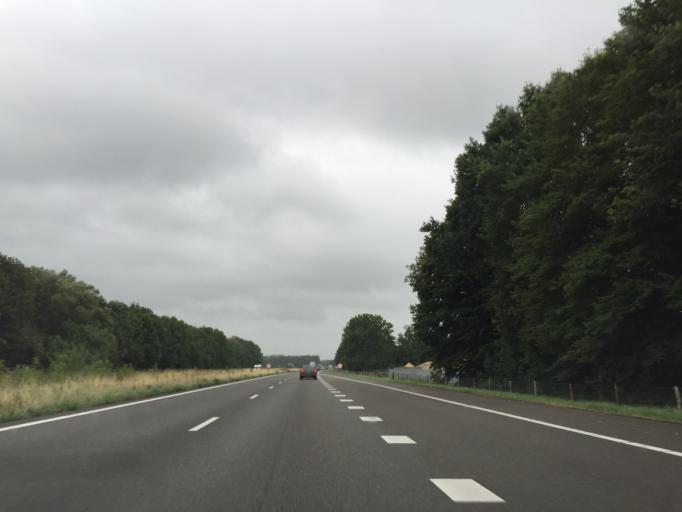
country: NL
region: Limburg
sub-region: Gemeente Maastricht
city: Heer
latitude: 50.8097
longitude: 5.7234
